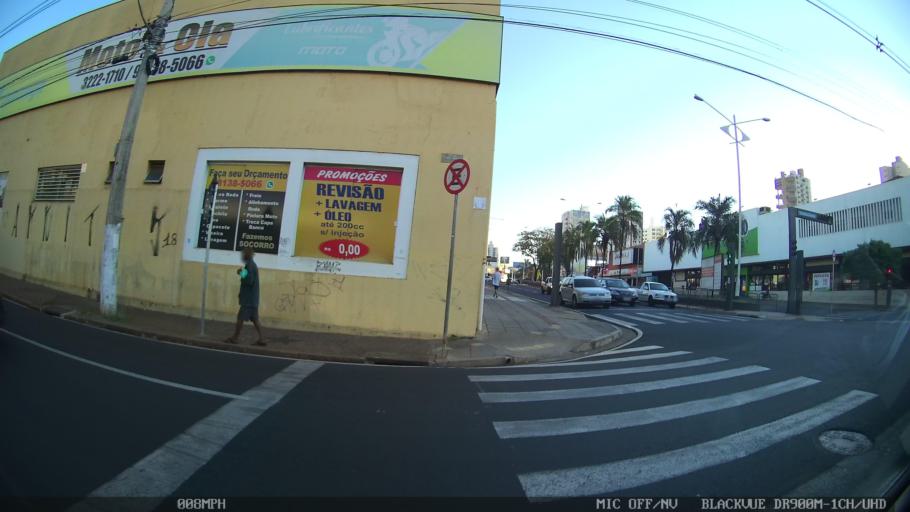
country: BR
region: Sao Paulo
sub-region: Sao Jose Do Rio Preto
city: Sao Jose do Rio Preto
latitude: -20.8071
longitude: -49.3798
